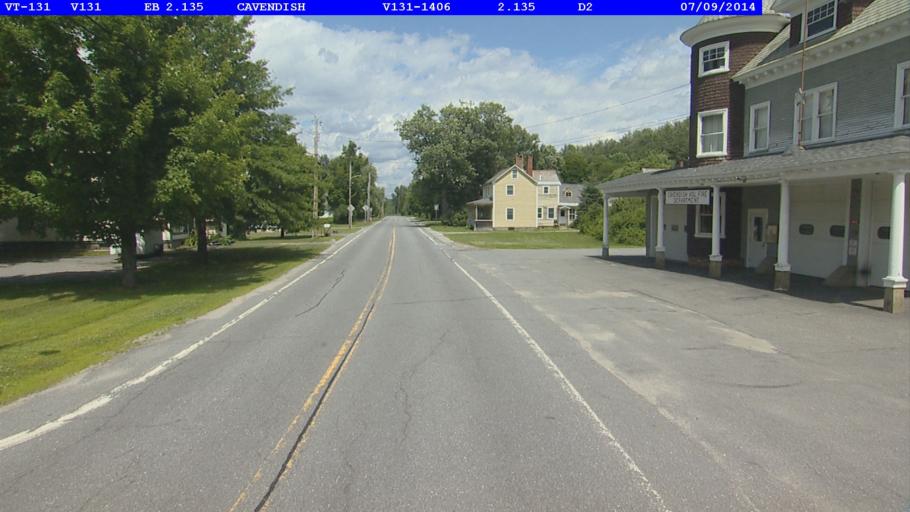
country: US
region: Vermont
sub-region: Windsor County
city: Chester
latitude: 43.3824
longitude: -72.6074
